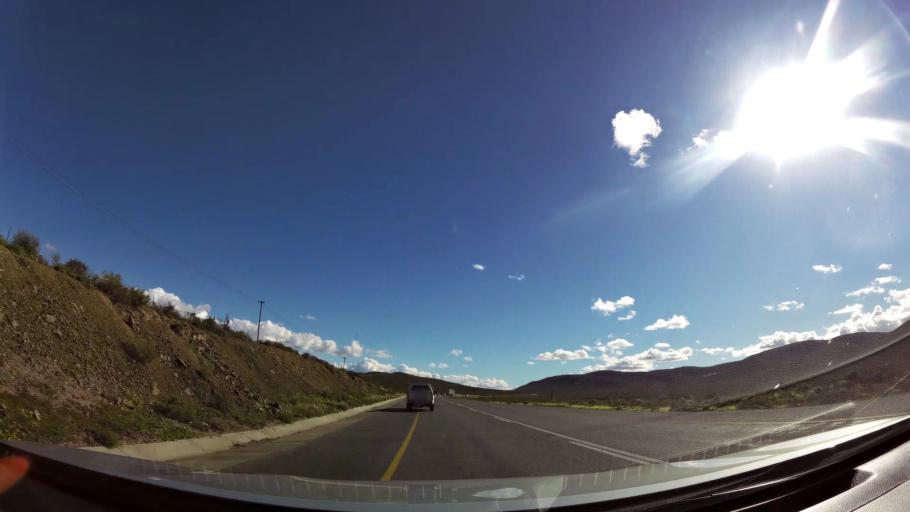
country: ZA
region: Western Cape
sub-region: Cape Winelands District Municipality
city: Worcester
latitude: -33.7377
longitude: 19.6837
